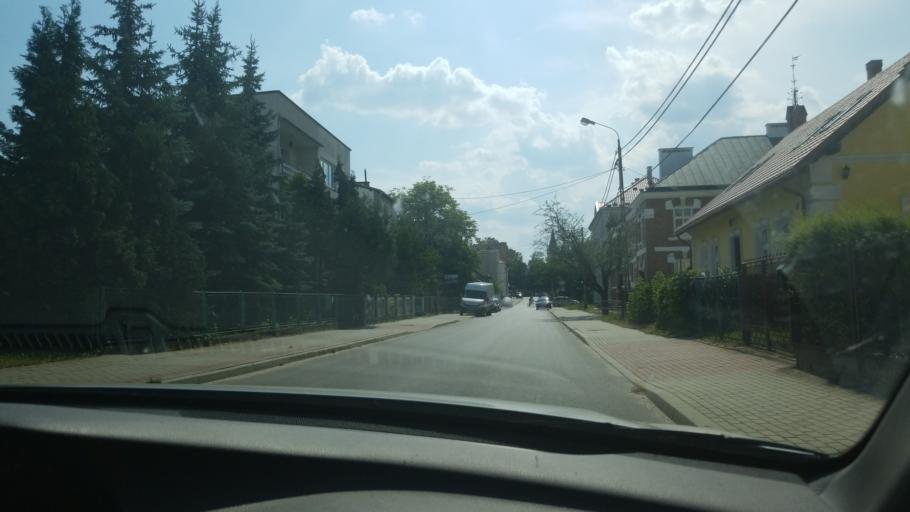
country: PL
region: Subcarpathian Voivodeship
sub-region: Powiat nizanski
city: Nisko
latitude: 50.5211
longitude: 22.1459
